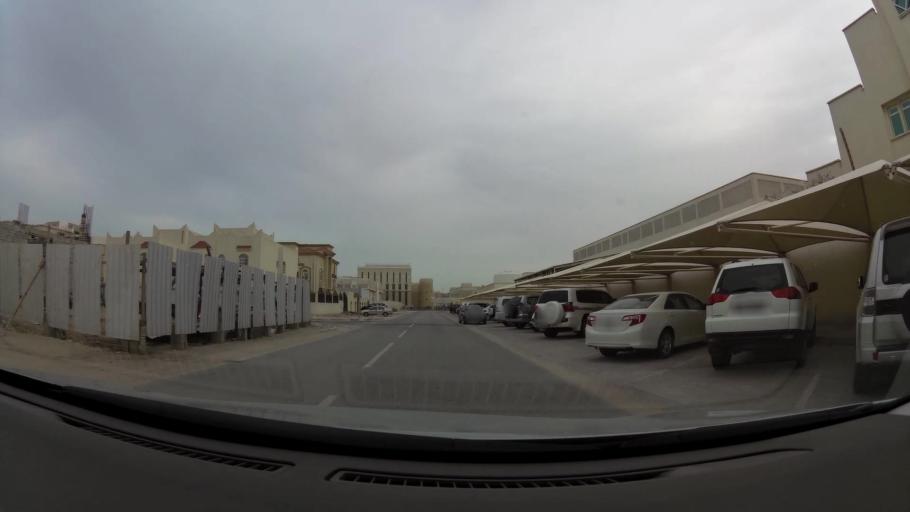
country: QA
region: Baladiyat ad Dawhah
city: Doha
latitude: 25.3082
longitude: 51.5013
